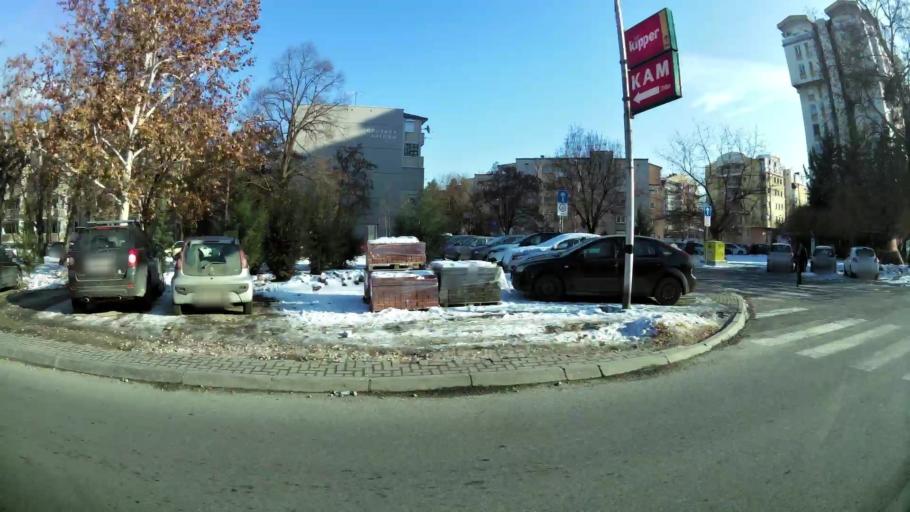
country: MK
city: Krushopek
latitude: 42.0062
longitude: 21.3832
